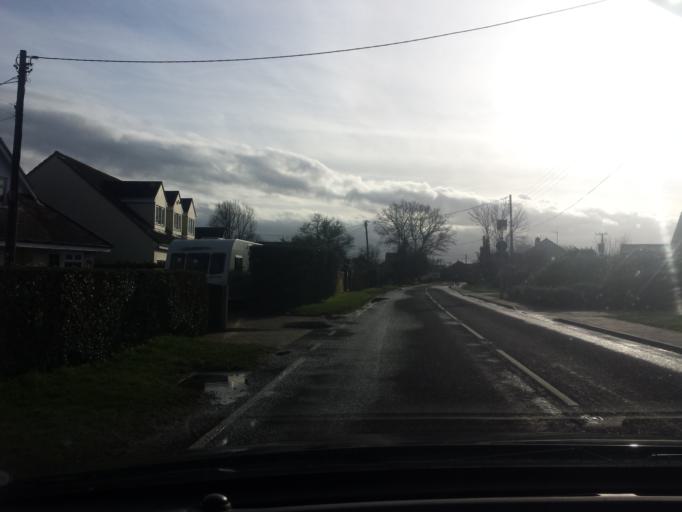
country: GB
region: England
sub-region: Essex
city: Great Bentley
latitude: 51.8719
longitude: 1.0354
